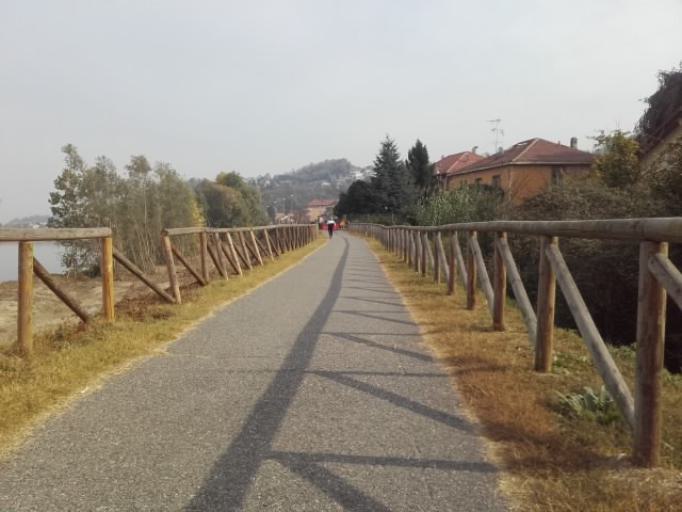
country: IT
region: Piedmont
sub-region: Provincia di Torino
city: San Mauro Torinese
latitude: 45.0978
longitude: 7.7580
